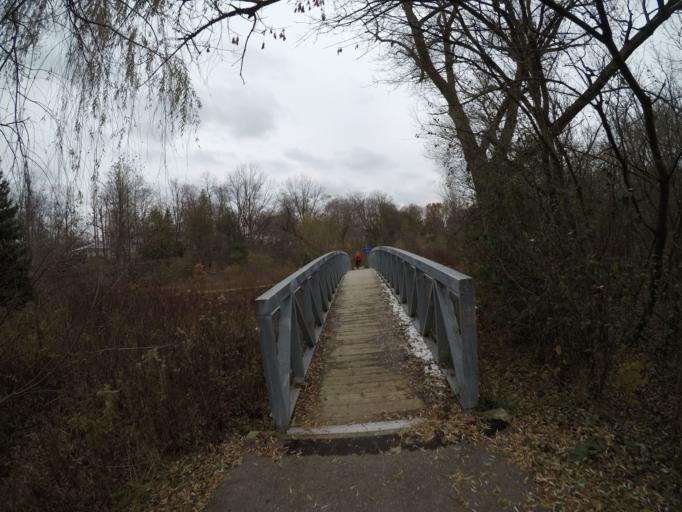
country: CA
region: Ontario
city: Waterloo
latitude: 43.4849
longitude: -80.5142
